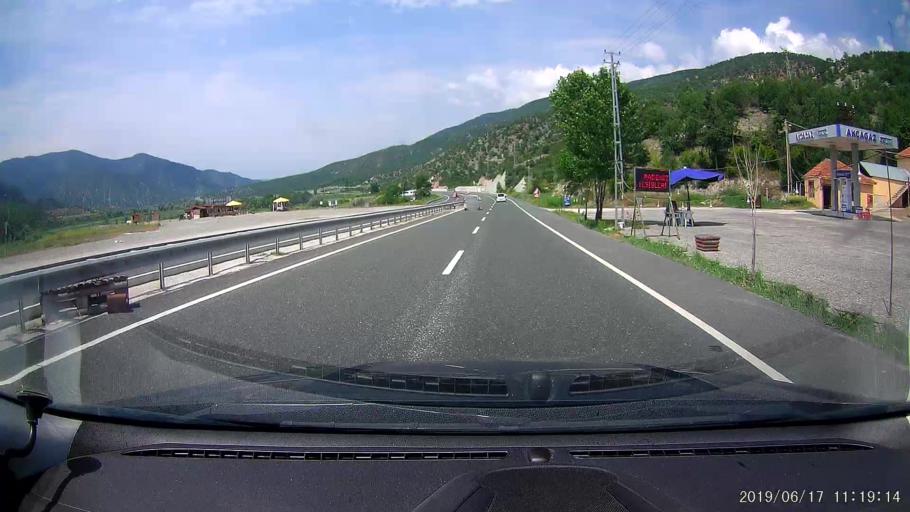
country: TR
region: Cankiri
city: Yaprakli
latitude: 40.9266
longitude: 33.8336
